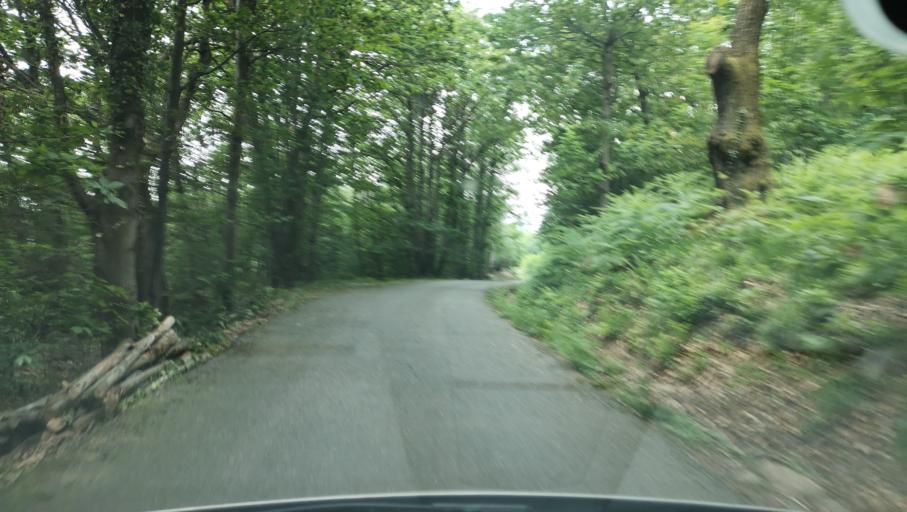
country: IT
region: Piedmont
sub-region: Provincia di Torino
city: Quassolo
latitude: 45.5303
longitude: 7.8277
